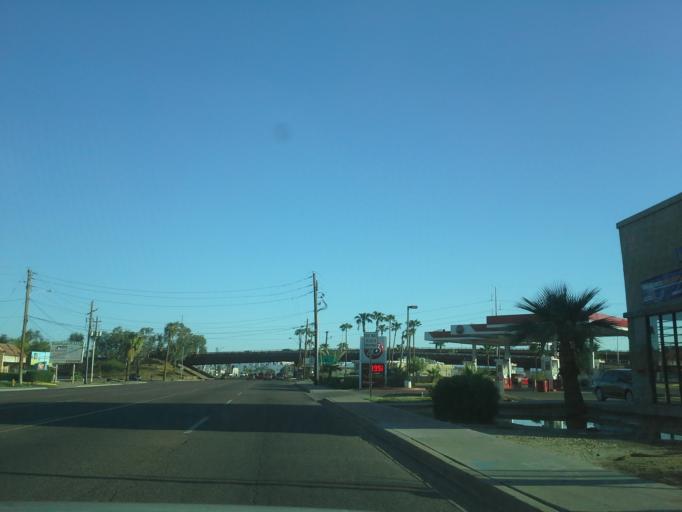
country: US
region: Arizona
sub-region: Maricopa County
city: Glendale
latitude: 33.4975
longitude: -112.1343
